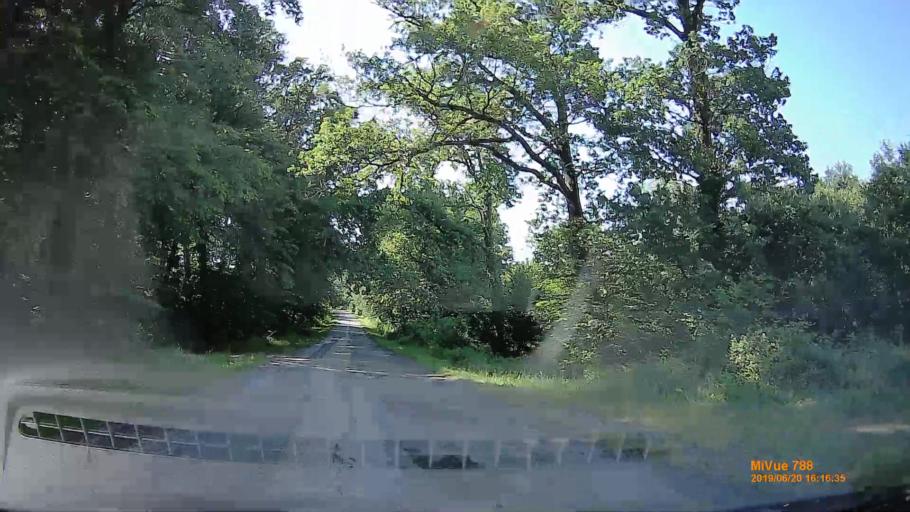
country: HU
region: Baranya
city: Buekkoesd
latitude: 46.0980
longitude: 18.0663
